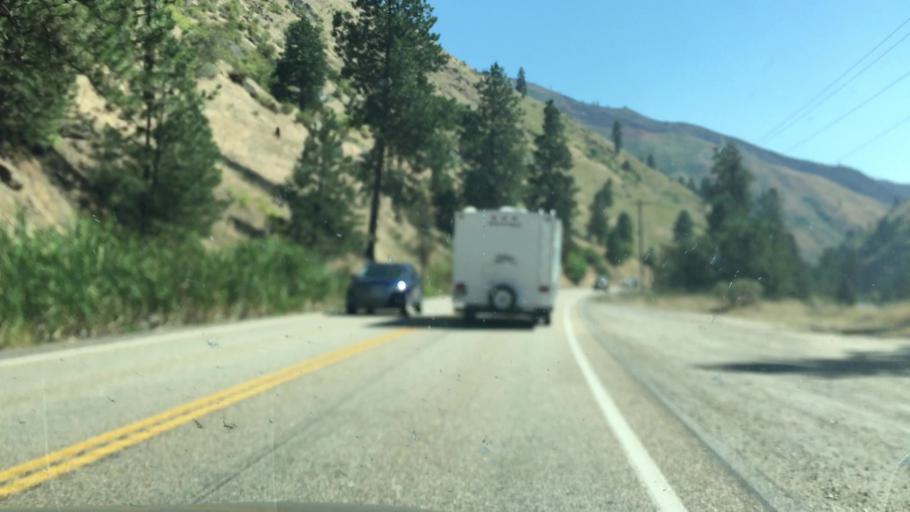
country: US
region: Idaho
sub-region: Boise County
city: Idaho City
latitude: 44.0446
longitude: -116.1304
